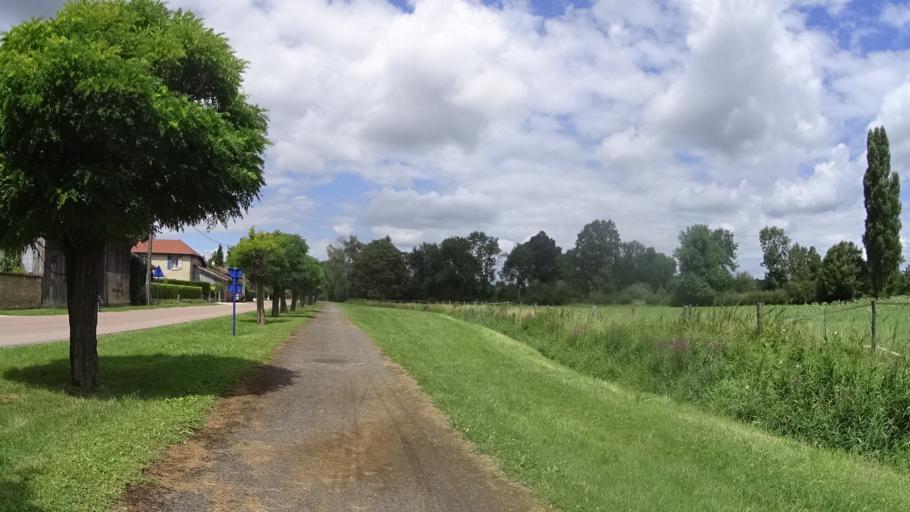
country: FR
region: Champagne-Ardenne
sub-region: Departement de la Haute-Marne
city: Montier-en-Der
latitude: 48.4740
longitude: 4.7641
